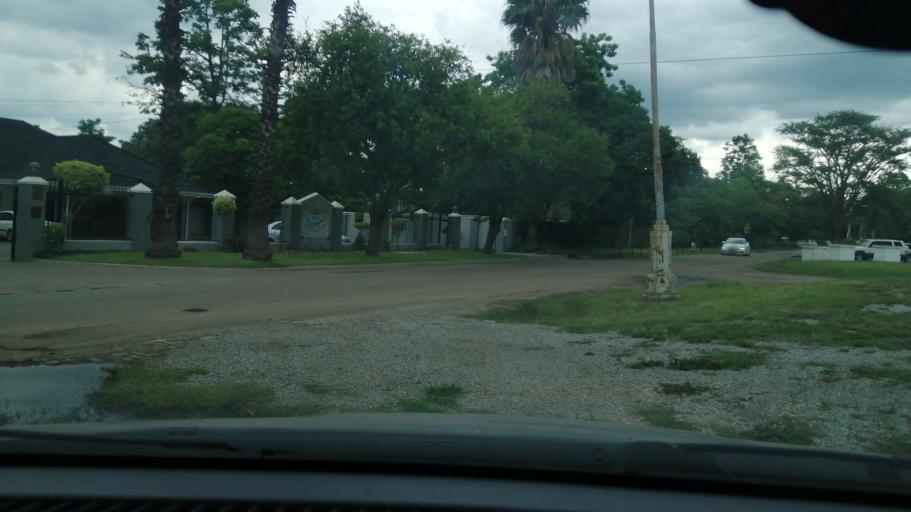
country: ZW
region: Harare
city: Harare
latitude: -17.8011
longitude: 31.0426
